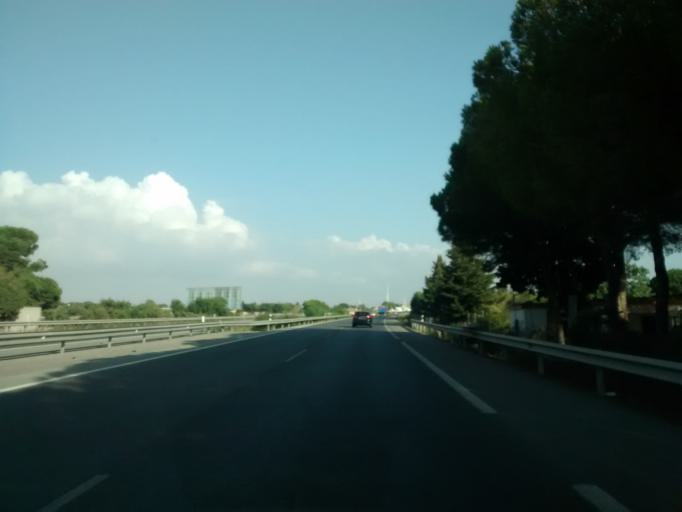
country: ES
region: Andalusia
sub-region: Provincia de Cadiz
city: Chiclana de la Frontera
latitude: 36.4419
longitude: -6.1320
